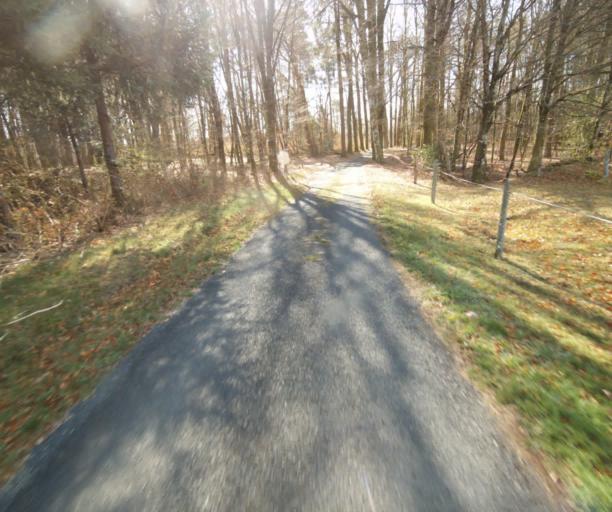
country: FR
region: Limousin
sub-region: Departement de la Correze
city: Laguenne
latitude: 45.2380
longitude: 1.9136
